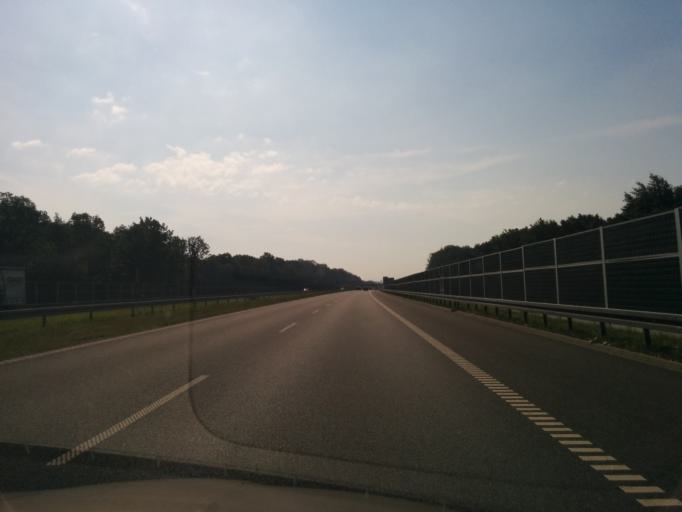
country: PL
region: Silesian Voivodeship
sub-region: Powiat tarnogorski
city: Radzionkow
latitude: 50.3805
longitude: 18.8666
